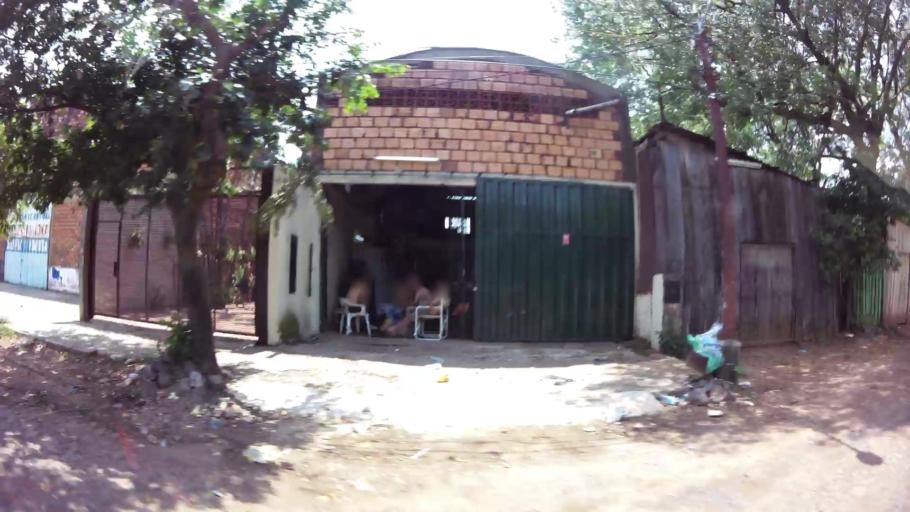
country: PY
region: Central
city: Fernando de la Mora
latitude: -25.3190
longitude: -57.5602
